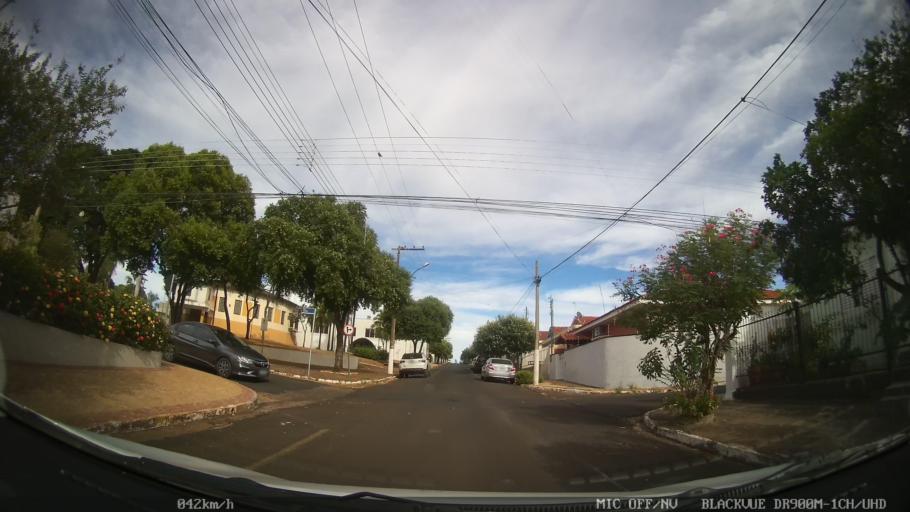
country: BR
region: Sao Paulo
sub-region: Catanduva
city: Catanduva
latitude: -21.1454
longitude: -48.9823
